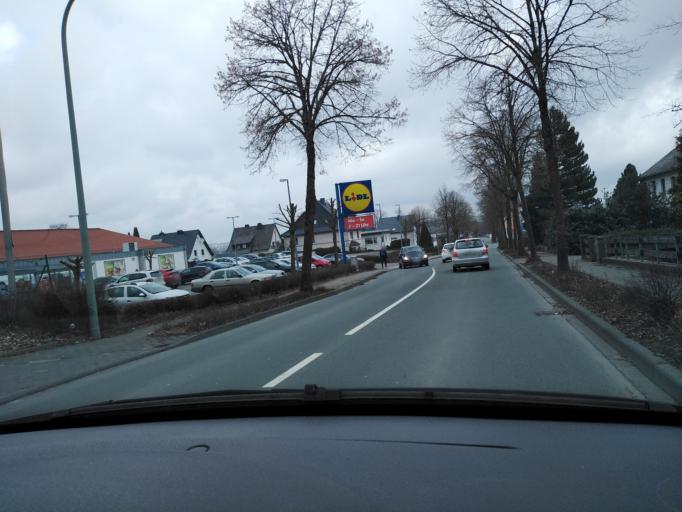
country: DE
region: North Rhine-Westphalia
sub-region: Regierungsbezirk Arnsberg
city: Brilon
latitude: 51.4032
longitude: 8.5716
